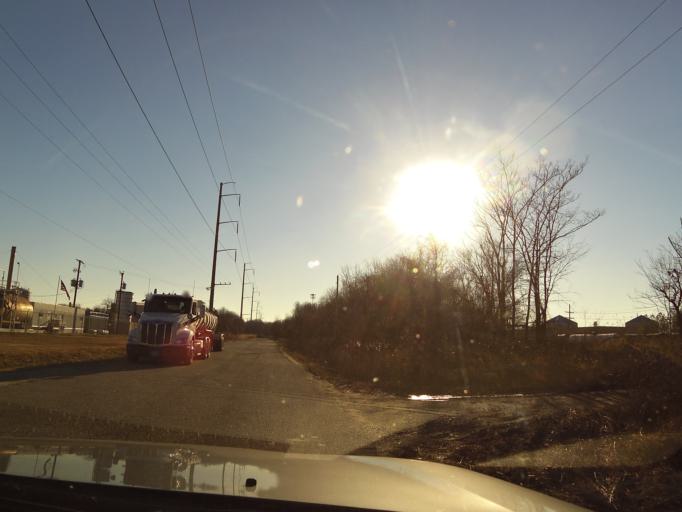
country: US
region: Virginia
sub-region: City of Hopewell
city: Hopewell
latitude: 37.2918
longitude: -77.2785
